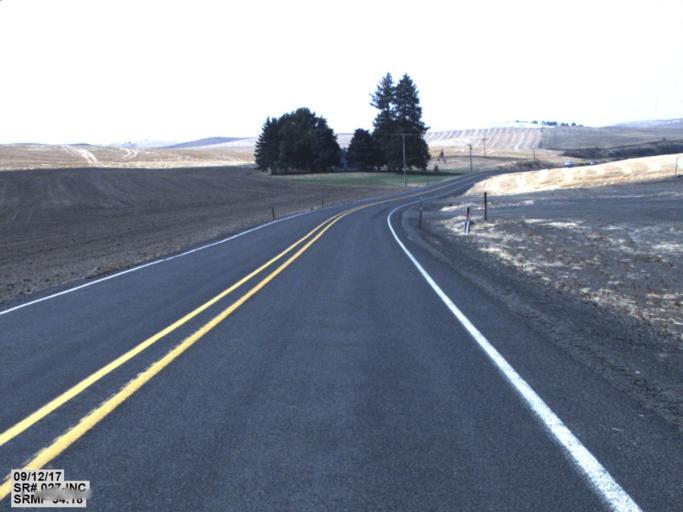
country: US
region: Idaho
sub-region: Benewah County
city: Plummer
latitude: 47.2744
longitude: -117.1358
